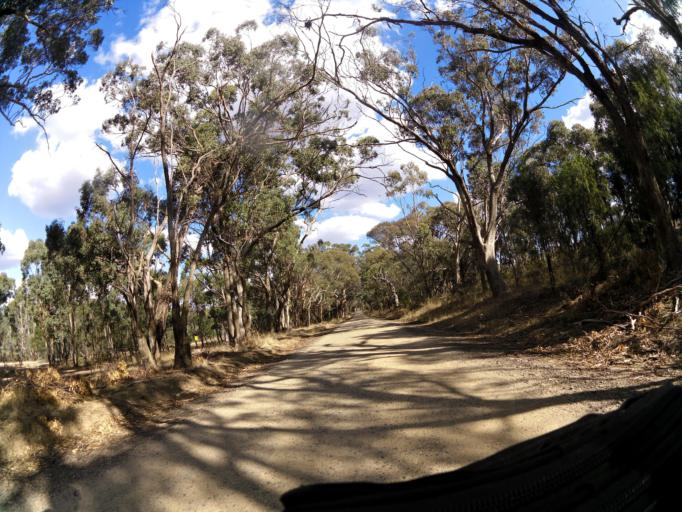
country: AU
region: Victoria
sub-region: Greater Bendigo
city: Kennington
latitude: -37.0003
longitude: 144.8118
